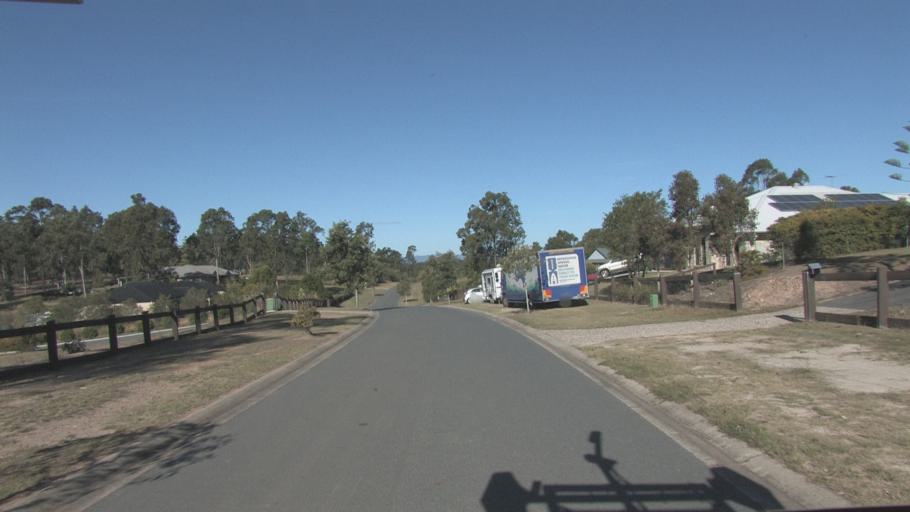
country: AU
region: Queensland
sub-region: Ipswich
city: Springfield Lakes
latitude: -27.7200
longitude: 152.9210
